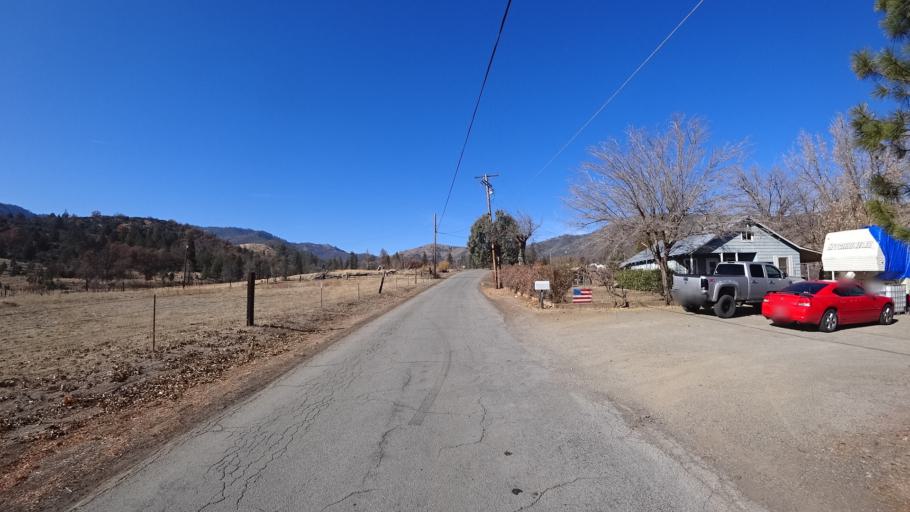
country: US
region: California
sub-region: Siskiyou County
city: Yreka
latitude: 41.7637
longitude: -122.6264
